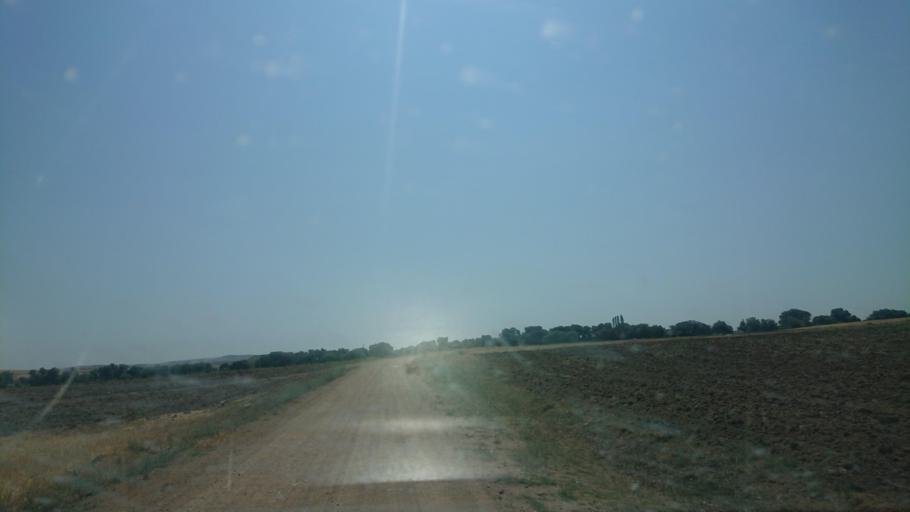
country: TR
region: Aksaray
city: Agacoren
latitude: 38.9547
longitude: 33.9380
